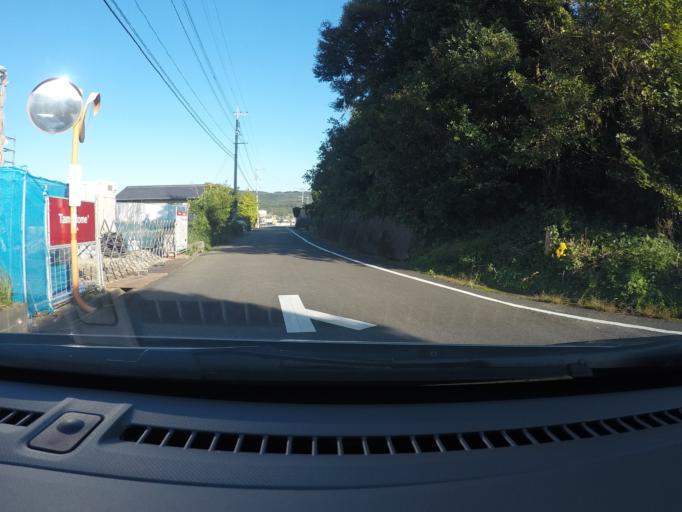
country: JP
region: Kumamoto
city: Minamata
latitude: 32.1768
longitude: 130.3712
